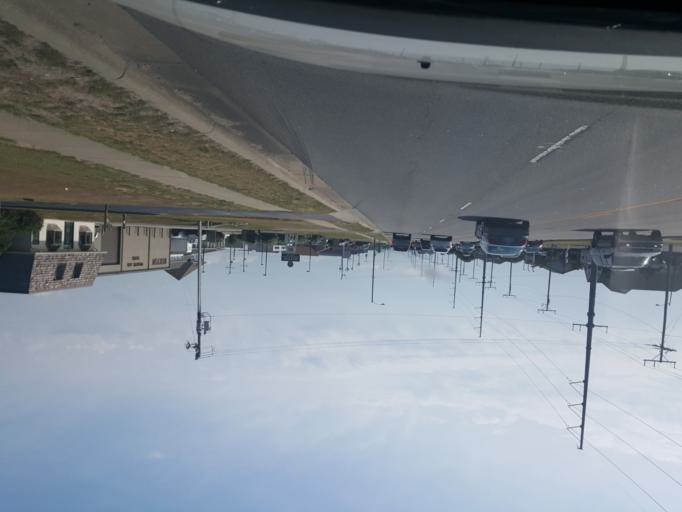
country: US
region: North Carolina
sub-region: Dare County
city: Kill Devil Hills
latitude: 36.0502
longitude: -75.6833
